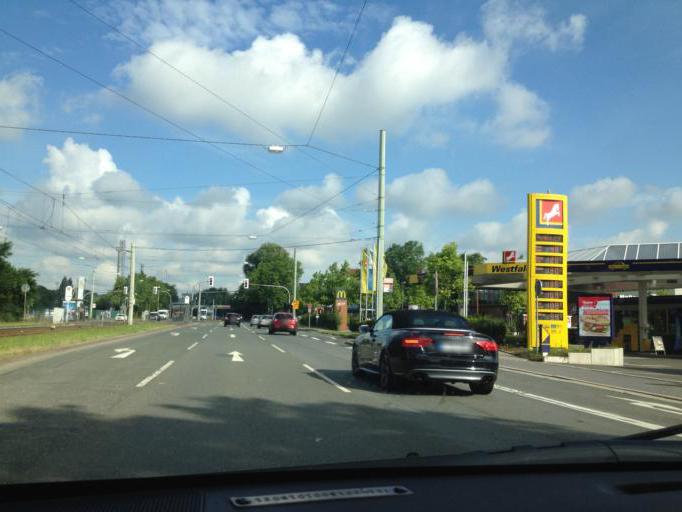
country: DE
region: North Rhine-Westphalia
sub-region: Regierungsbezirk Arnsberg
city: Bochum
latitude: 51.4678
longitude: 7.2709
